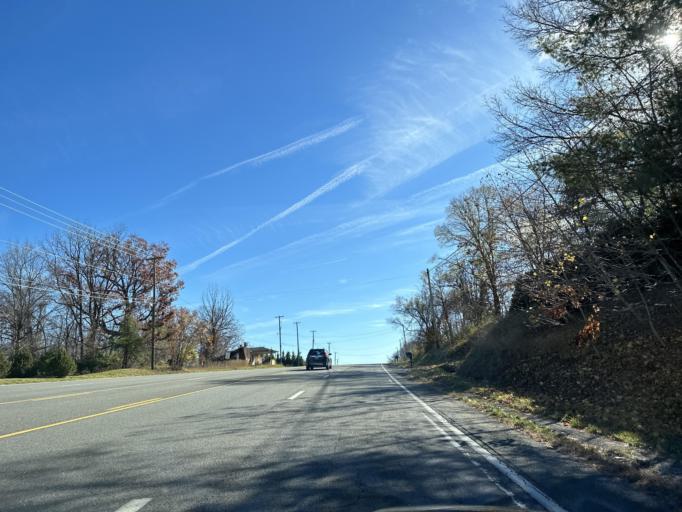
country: US
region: Virginia
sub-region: Augusta County
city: Fishersville
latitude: 38.1080
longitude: -78.9880
